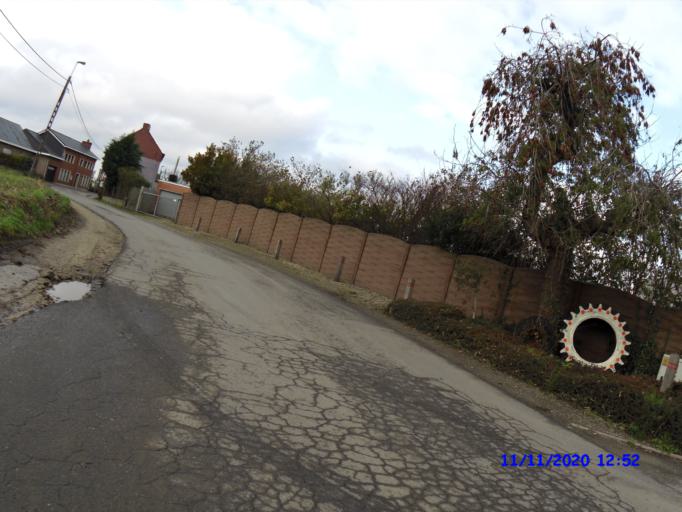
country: BE
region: Flanders
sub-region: Provincie Oost-Vlaanderen
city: Dendermonde
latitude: 51.0196
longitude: 4.0540
